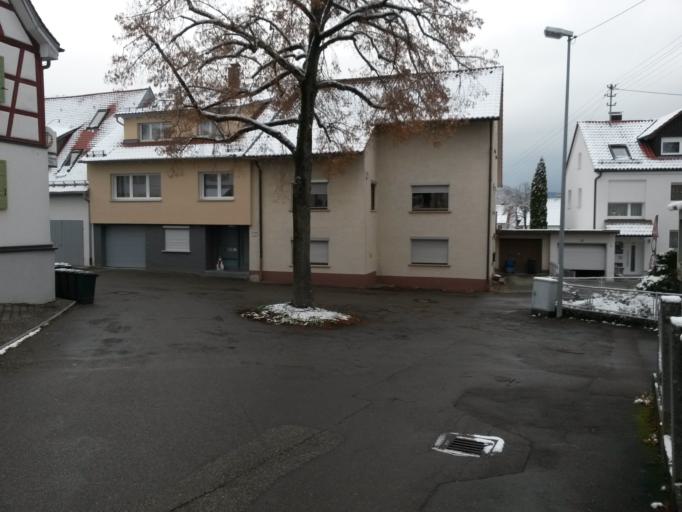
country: DE
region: Baden-Wuerttemberg
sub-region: Regierungsbezirk Stuttgart
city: Bad Uberkingen
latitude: 48.5994
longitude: 9.7976
